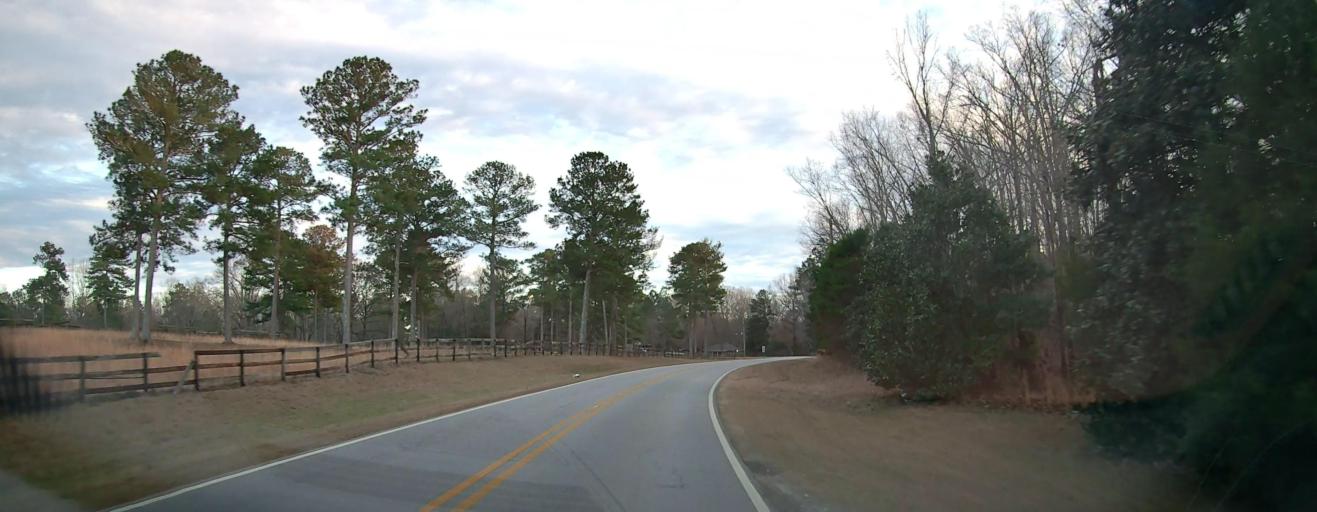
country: US
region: Georgia
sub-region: Harris County
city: Hamilton
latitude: 32.6014
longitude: -84.8784
